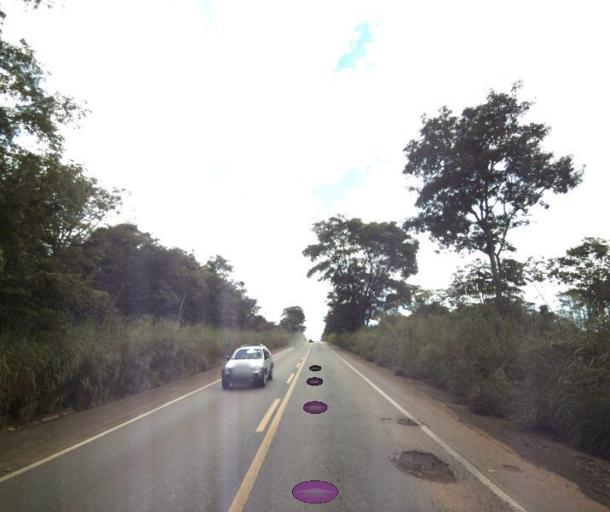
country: BR
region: Goias
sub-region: Petrolina De Goias
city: Petrolina de Goias
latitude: -15.9398
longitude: -49.1974
